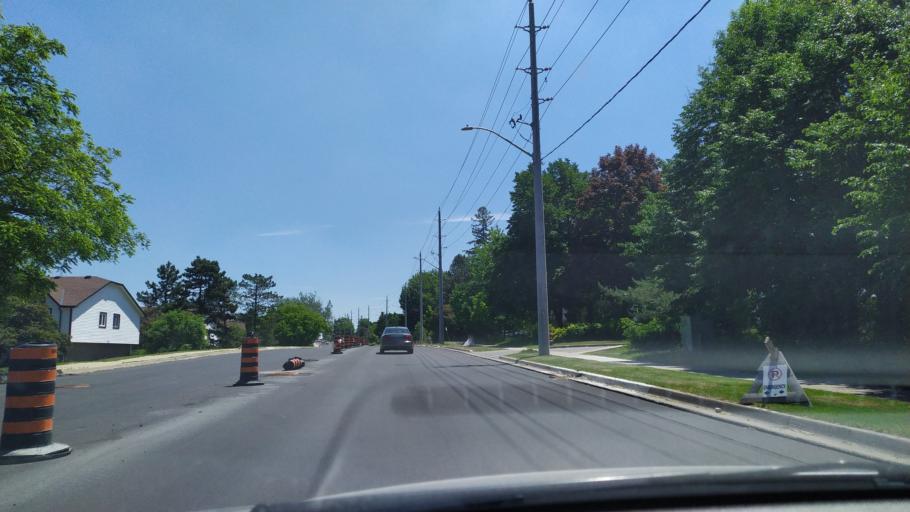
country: CA
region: Ontario
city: Kitchener
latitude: 43.3945
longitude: -80.4451
